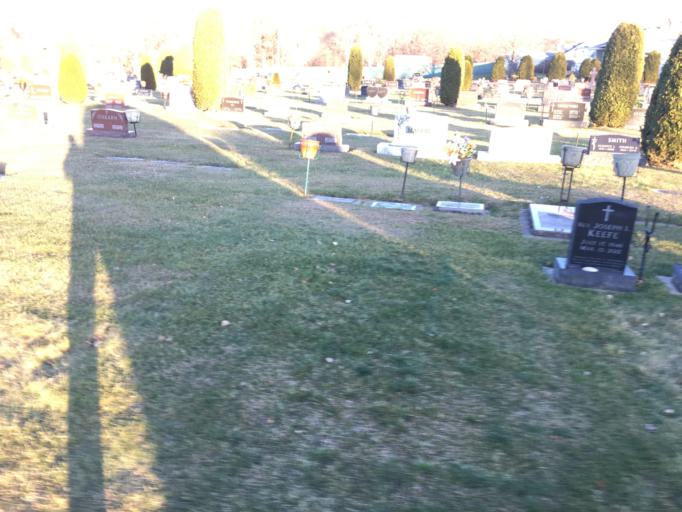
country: US
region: Minnesota
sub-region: Olmsted County
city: Rochester
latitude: 44.0283
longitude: -92.4460
